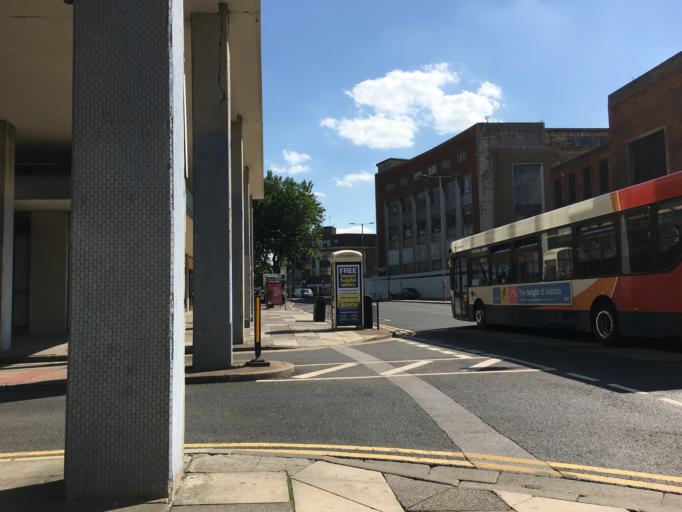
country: GB
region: England
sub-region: City of Kingston upon Hull
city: Hull
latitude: 53.7464
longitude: -0.3394
